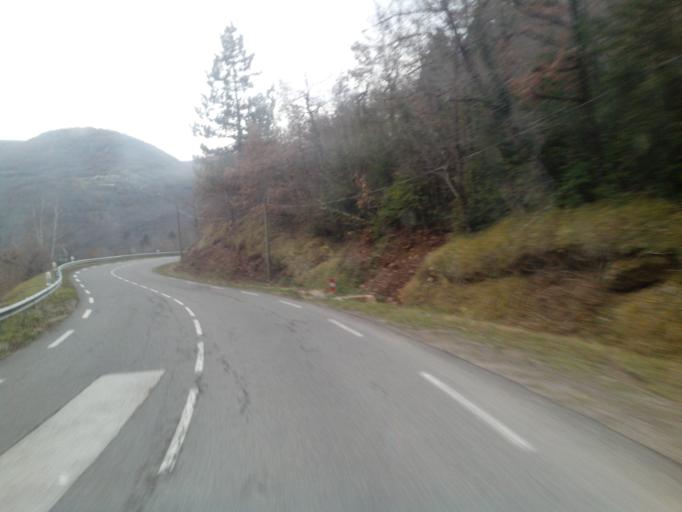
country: FR
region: Languedoc-Roussillon
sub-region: Departement de la Lozere
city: Florac
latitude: 44.2943
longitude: 3.5956
